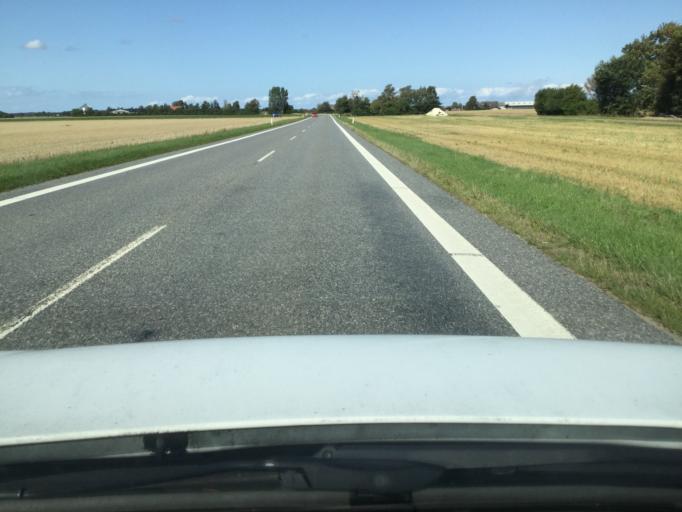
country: DK
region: Zealand
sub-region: Lolland Kommune
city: Rodby
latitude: 54.7309
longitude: 11.3885
